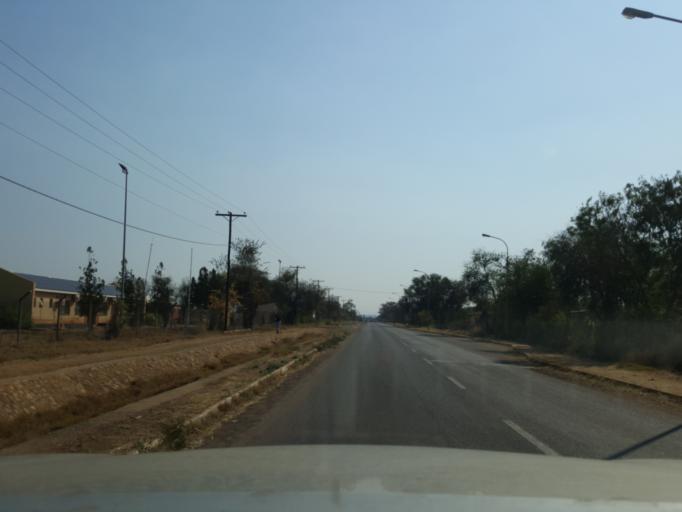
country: BW
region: South East
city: Lobatse
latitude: -25.2011
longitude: 25.6894
